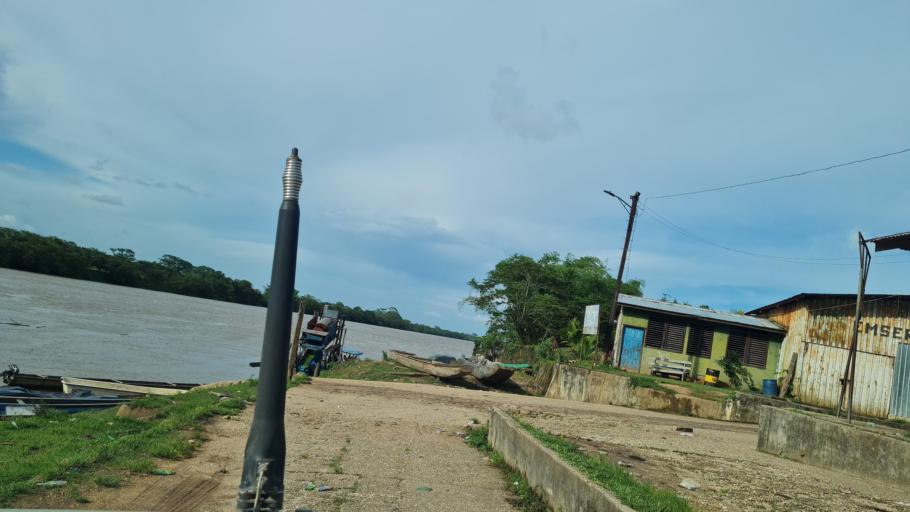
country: NI
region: Atlantico Norte (RAAN)
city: Waspam
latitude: 14.7477
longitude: -83.9690
